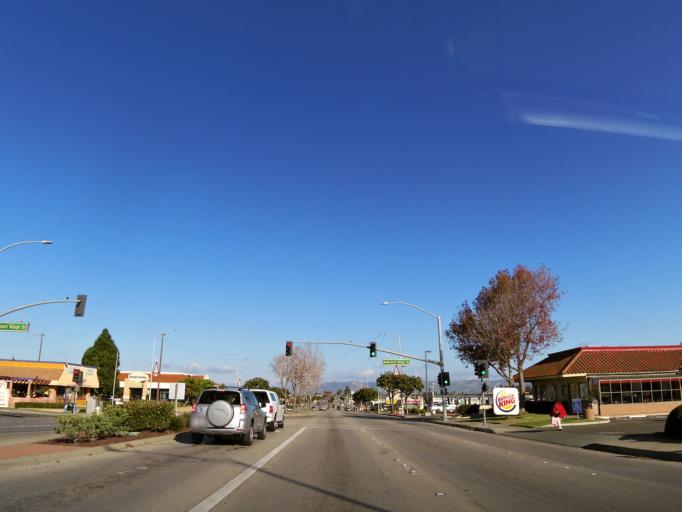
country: US
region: California
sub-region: Santa Barbara County
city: Santa Maria
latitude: 34.9226
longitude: -120.4360
